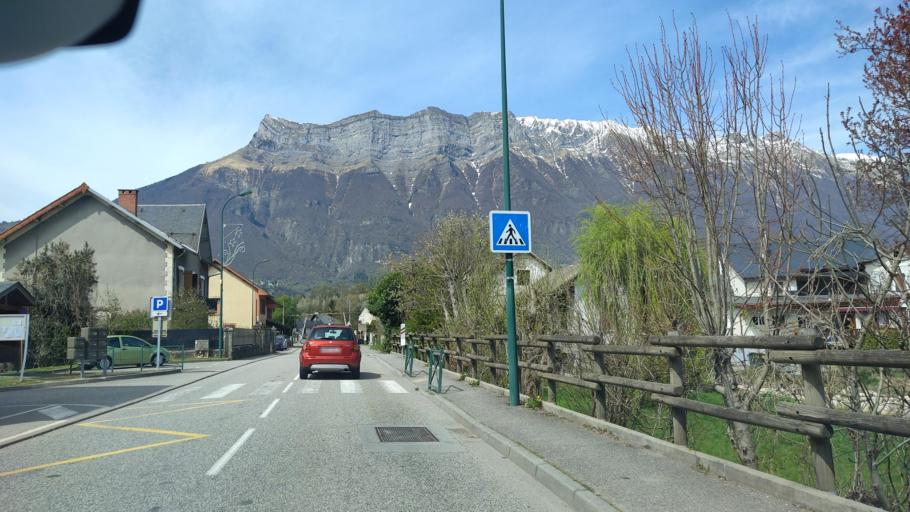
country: FR
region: Rhone-Alpes
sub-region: Departement de la Savoie
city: Aiton
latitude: 45.5564
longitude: 6.2058
